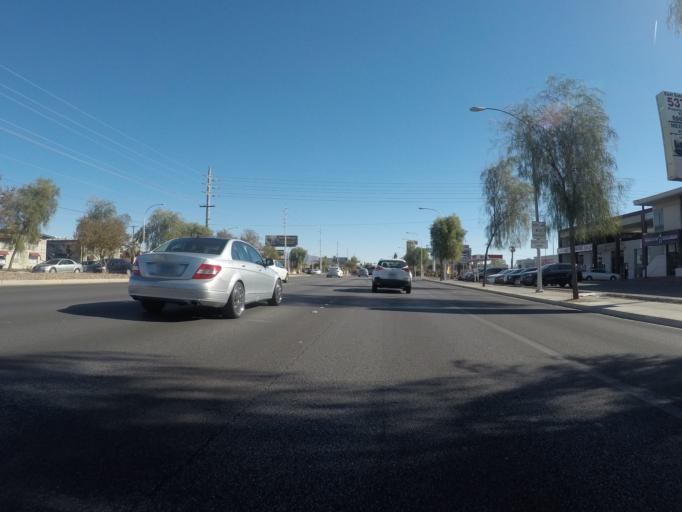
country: US
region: Nevada
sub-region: Clark County
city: Winchester
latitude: 36.1437
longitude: -115.1494
